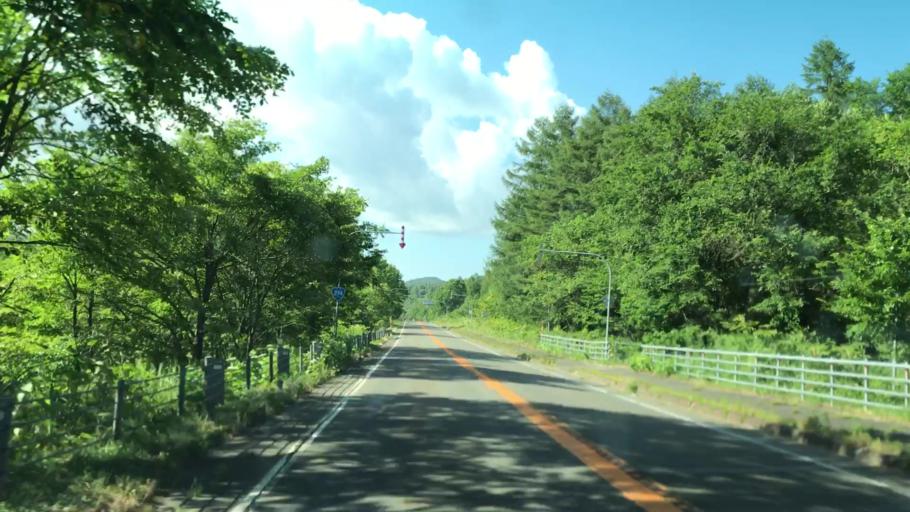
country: JP
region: Hokkaido
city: Shimo-furano
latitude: 42.8898
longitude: 142.4313
